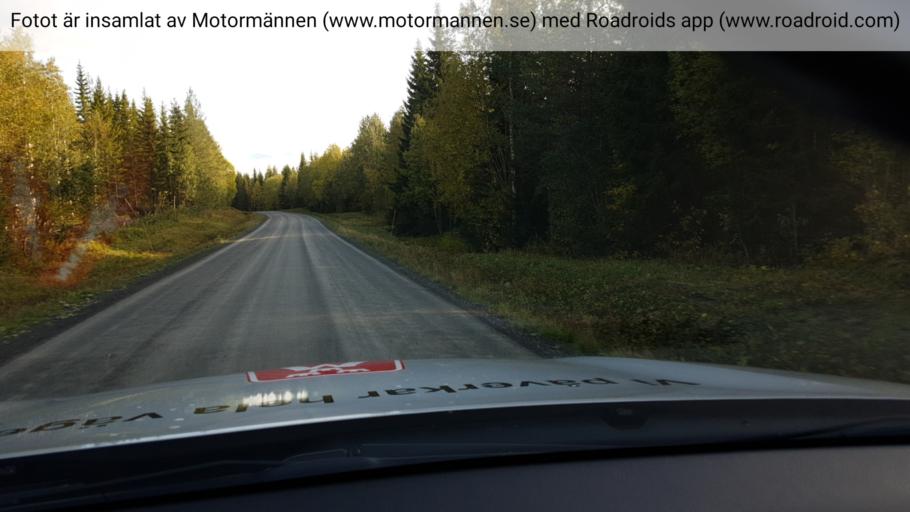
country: SE
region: Jaemtland
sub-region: Krokoms Kommun
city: Krokom
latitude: 63.7111
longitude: 14.5245
